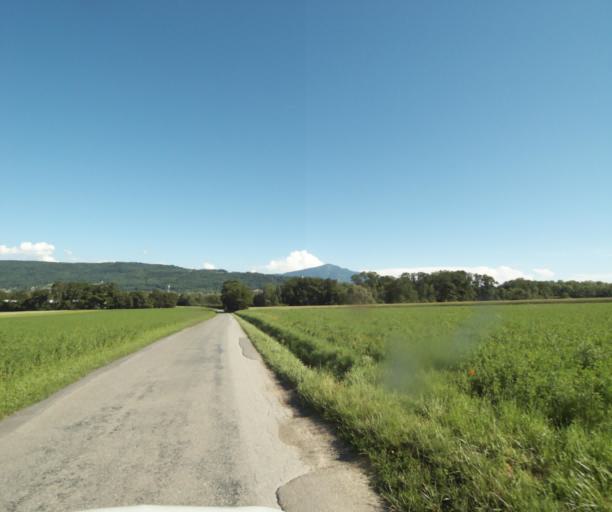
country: FR
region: Rhone-Alpes
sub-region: Departement de la Haute-Savoie
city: Douvaine
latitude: 46.3289
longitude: 6.3115
